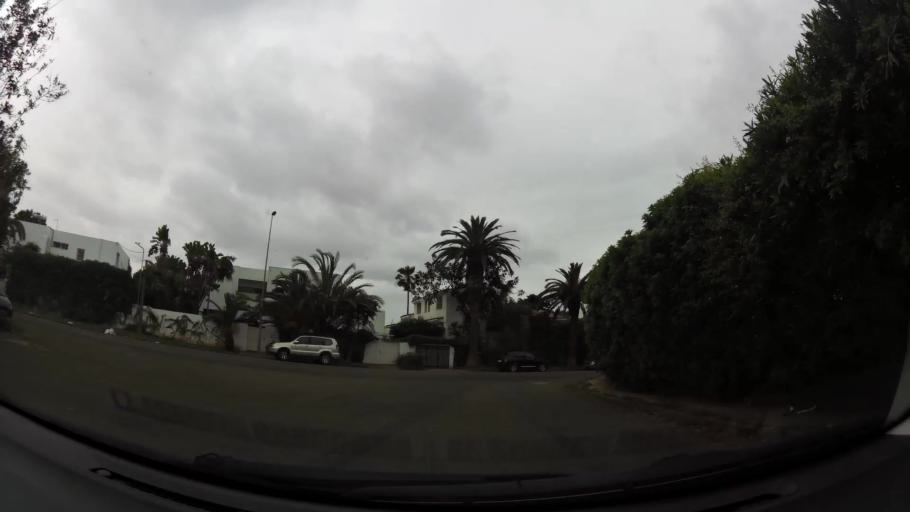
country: MA
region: Grand Casablanca
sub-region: Casablanca
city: Casablanca
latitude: 33.5946
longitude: -7.6655
